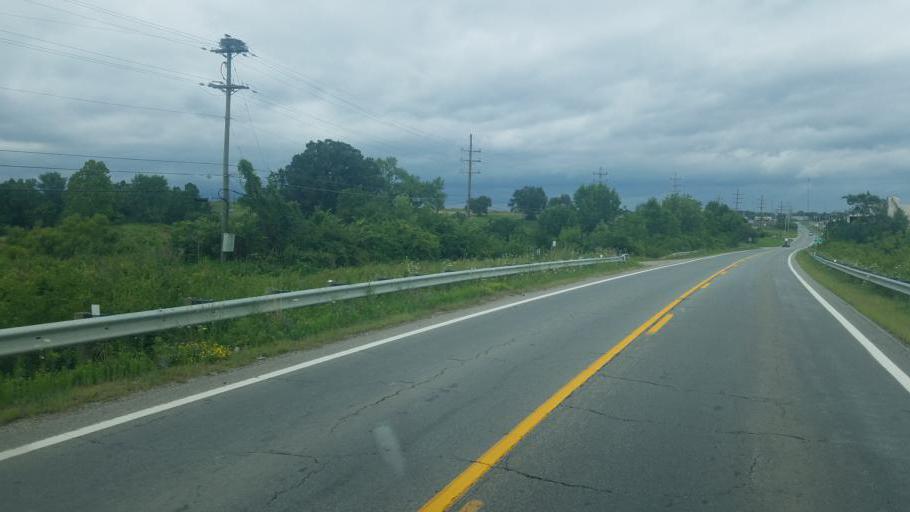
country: US
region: Ohio
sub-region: Franklin County
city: Grove City
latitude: 39.8871
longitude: -83.0278
